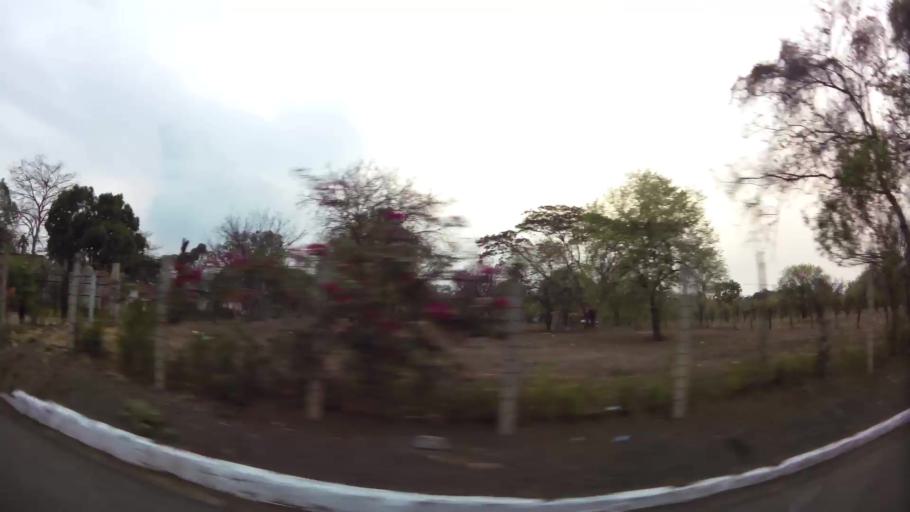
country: NI
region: Masaya
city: Nindiri
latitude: 12.0013
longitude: -86.1241
